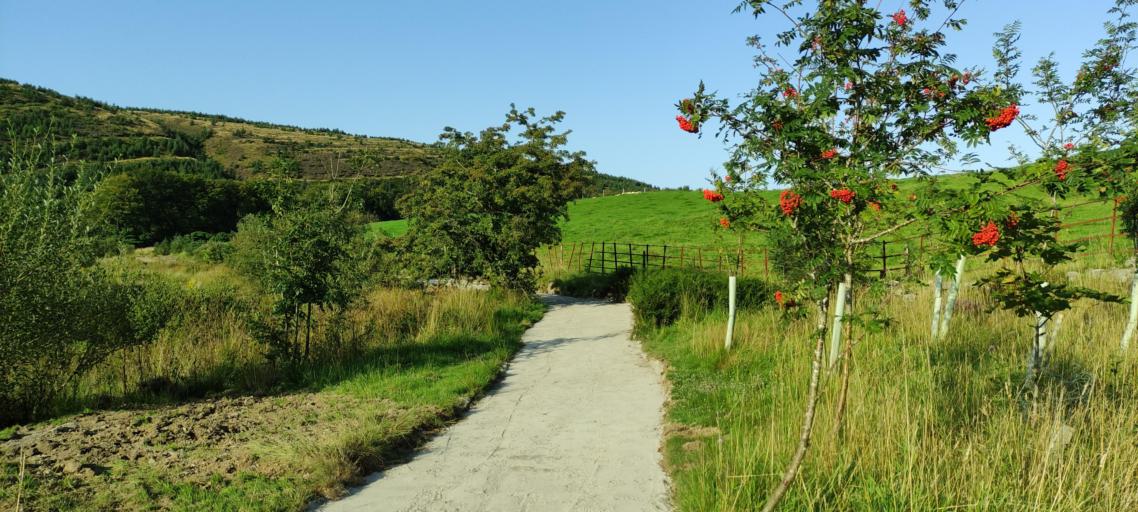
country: GB
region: England
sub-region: Cumbria
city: Frizington
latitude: 54.5650
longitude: -3.4027
